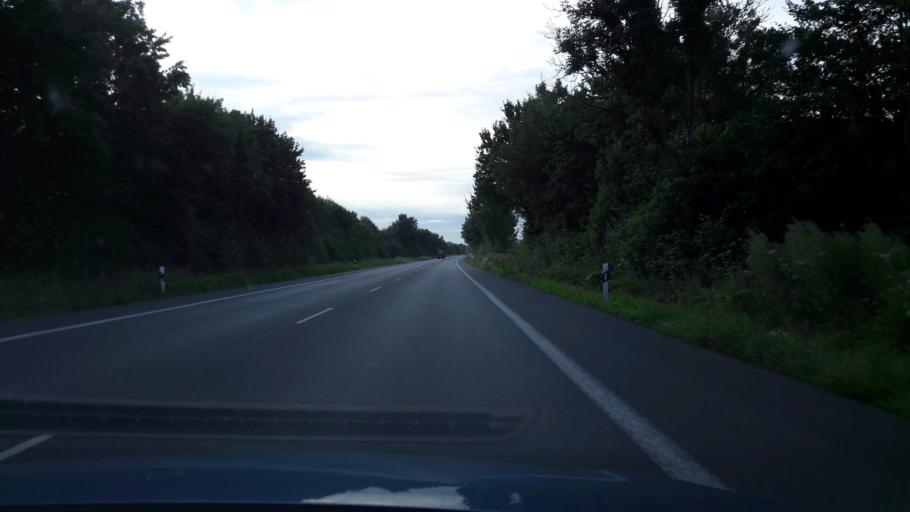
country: DE
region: North Rhine-Westphalia
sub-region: Regierungsbezirk Munster
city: Telgte
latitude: 51.9340
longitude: 7.7405
